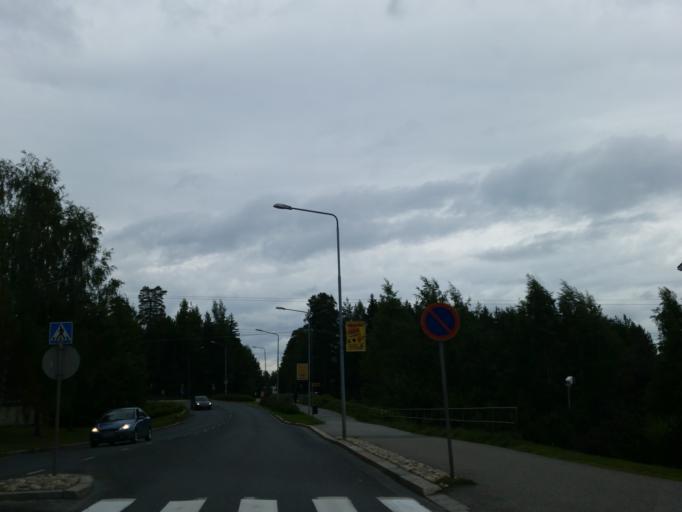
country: FI
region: Northern Savo
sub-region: Kuopio
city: Kuopio
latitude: 62.9033
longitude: 27.7060
